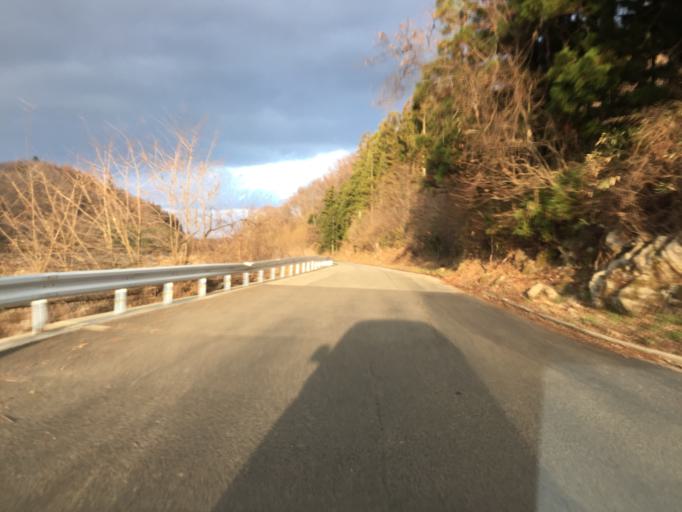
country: JP
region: Fukushima
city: Motomiya
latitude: 37.5397
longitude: 140.4212
